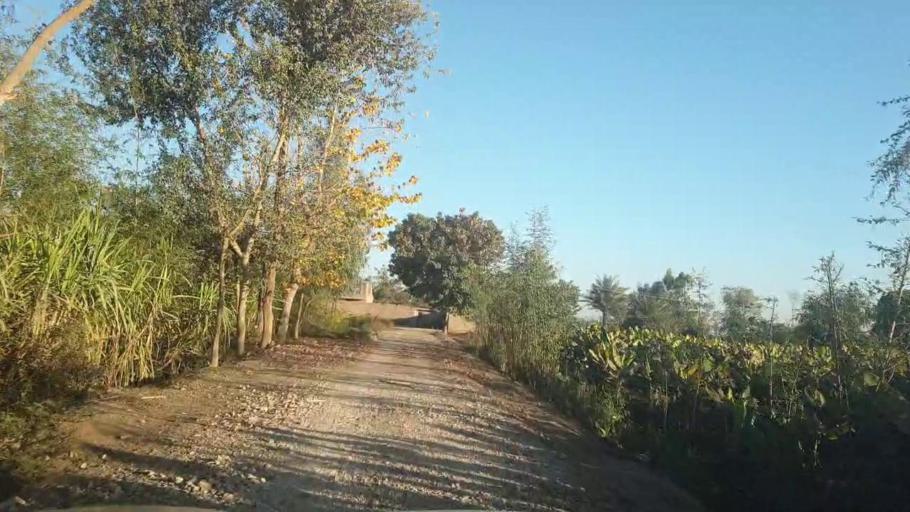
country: PK
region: Sindh
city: Ghotki
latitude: 28.0063
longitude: 69.2704
